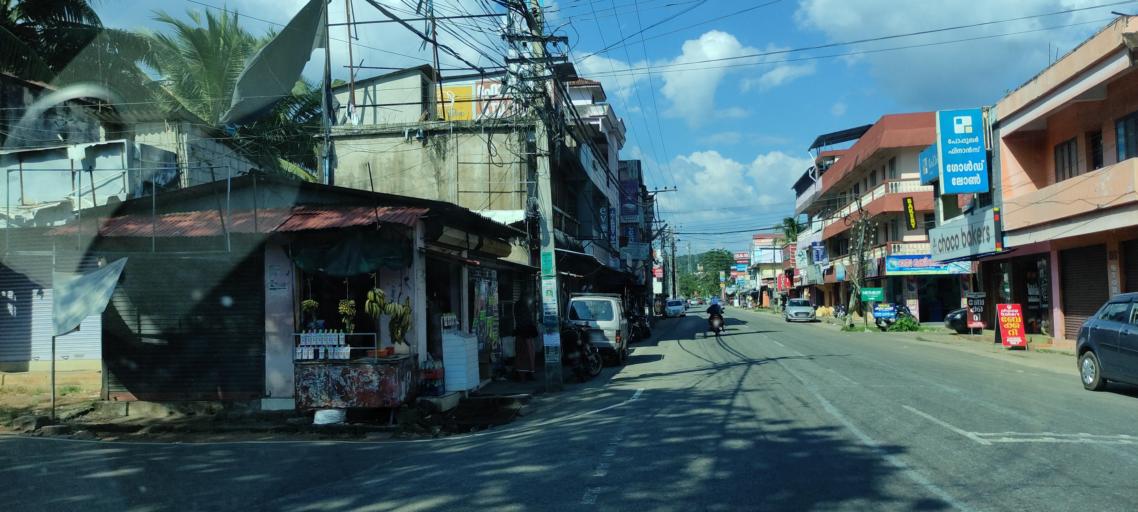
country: IN
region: Kerala
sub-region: Pattanamtitta
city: Pathanamthitta
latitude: 9.2402
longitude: 76.7554
